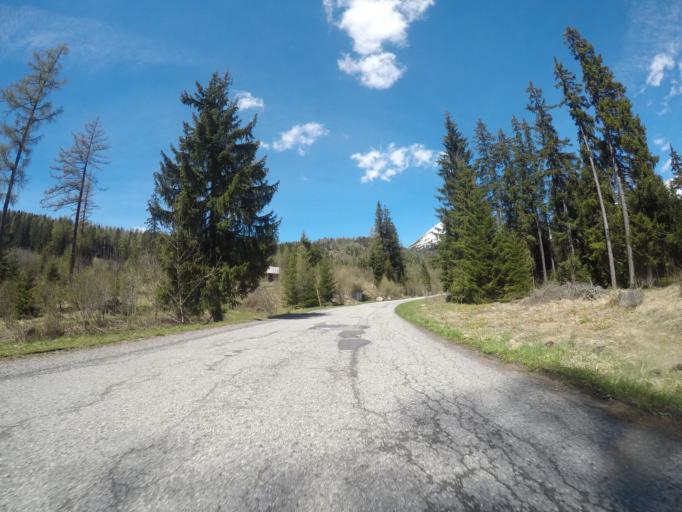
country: SK
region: Presovsky
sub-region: Okres Poprad
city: Strba
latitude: 49.1197
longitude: 20.0756
